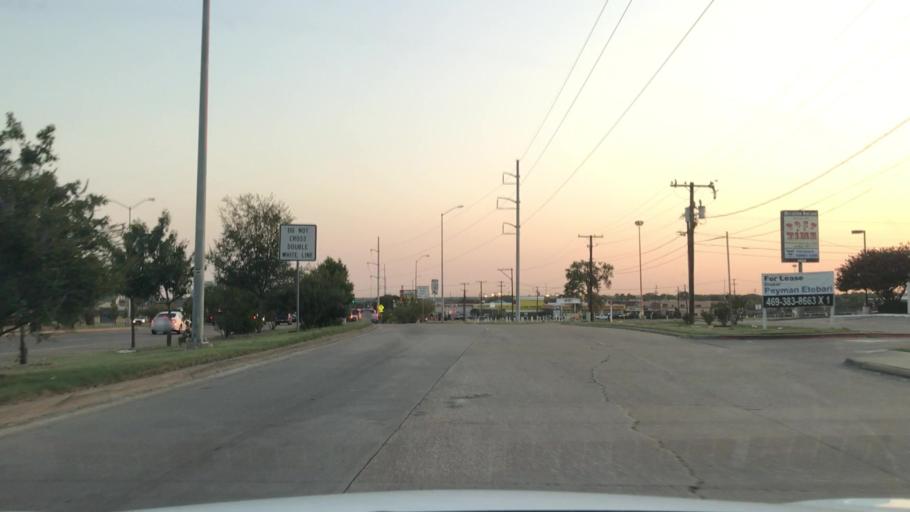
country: US
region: Texas
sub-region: Dallas County
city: Mesquite
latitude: 32.8005
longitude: -96.6822
